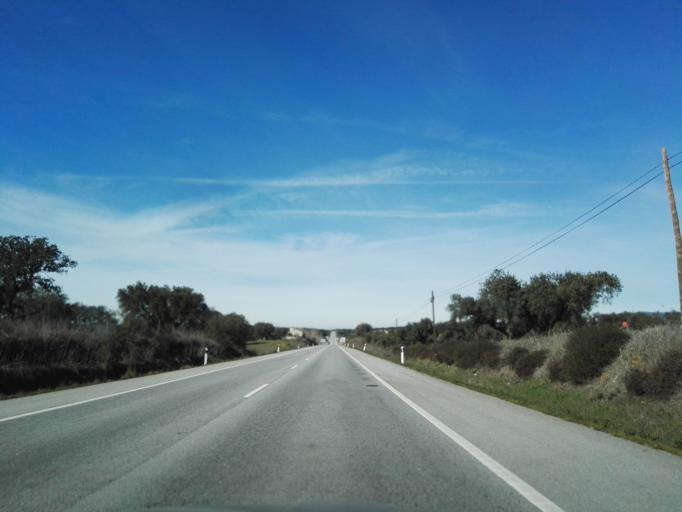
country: PT
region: Portalegre
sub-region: Arronches
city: Arronches
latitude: 39.1561
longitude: -7.3165
